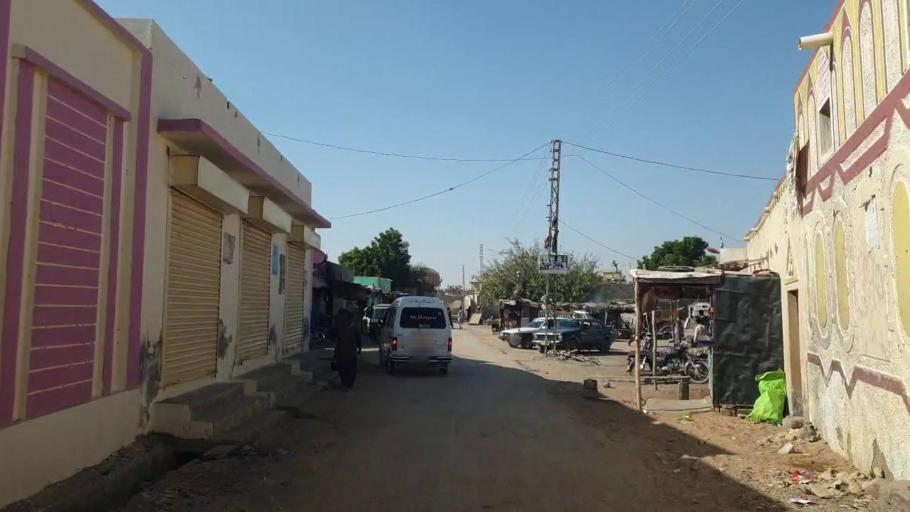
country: PK
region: Sindh
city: Jamshoro
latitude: 25.4100
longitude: 67.7853
